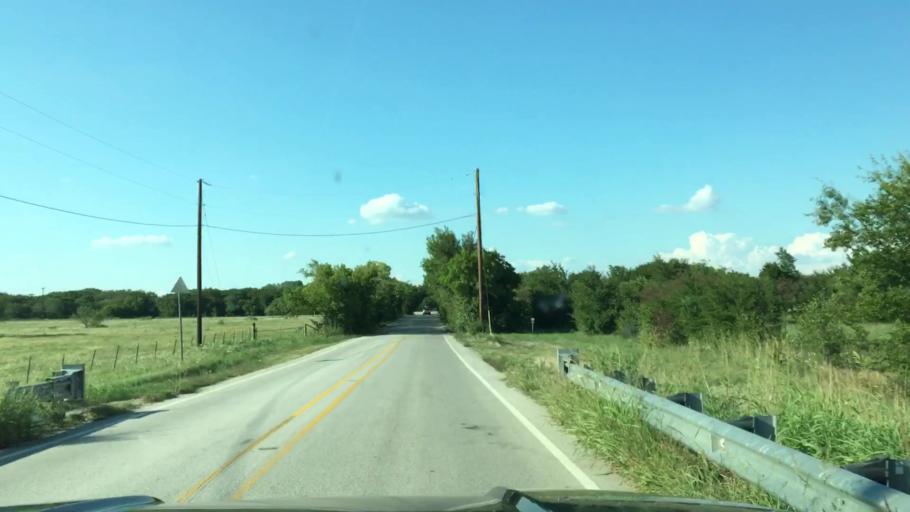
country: US
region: Texas
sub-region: Tarrant County
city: Haslet
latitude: 33.0329
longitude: -97.3745
